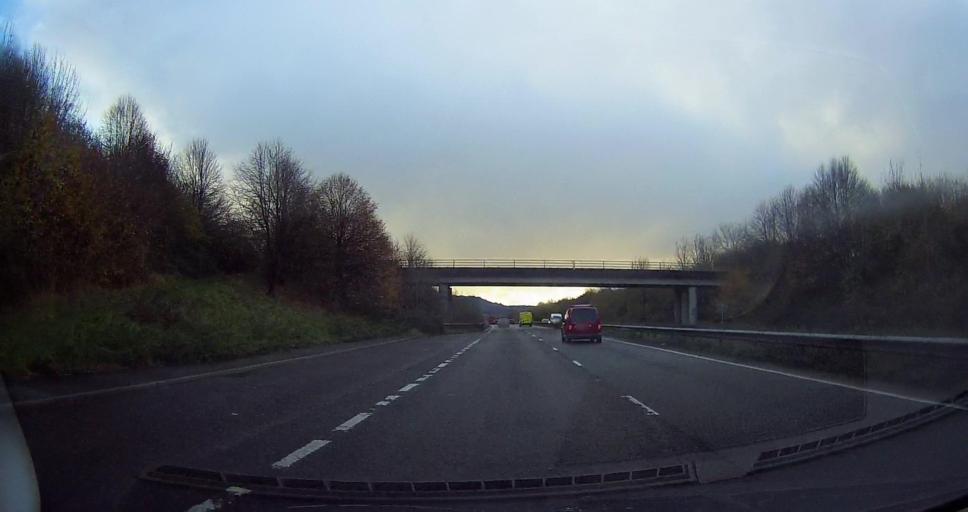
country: GB
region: England
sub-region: West Sussex
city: Hurstpierpoint
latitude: 50.9361
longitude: -0.1954
